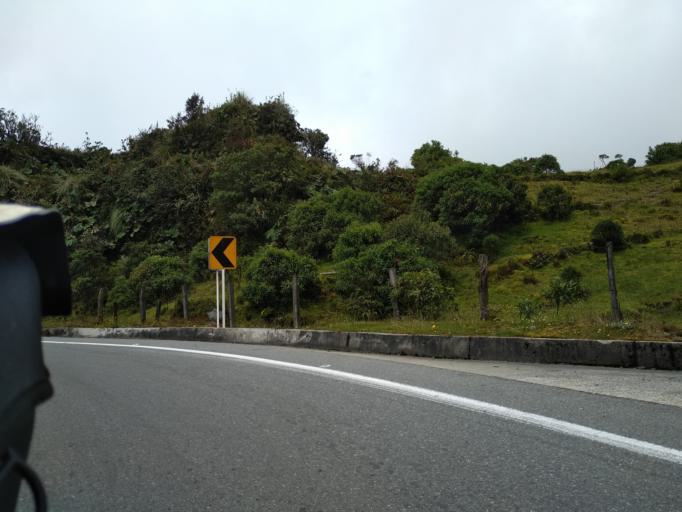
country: CO
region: Tolima
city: Herveo
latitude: 5.0729
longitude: -75.2854
